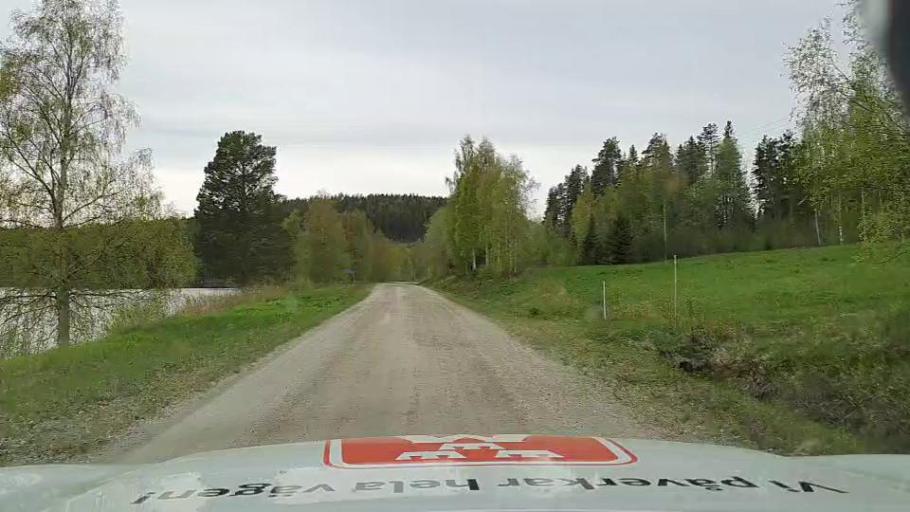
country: SE
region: Jaemtland
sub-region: Bergs Kommun
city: Hoverberg
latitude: 62.6881
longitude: 14.7830
